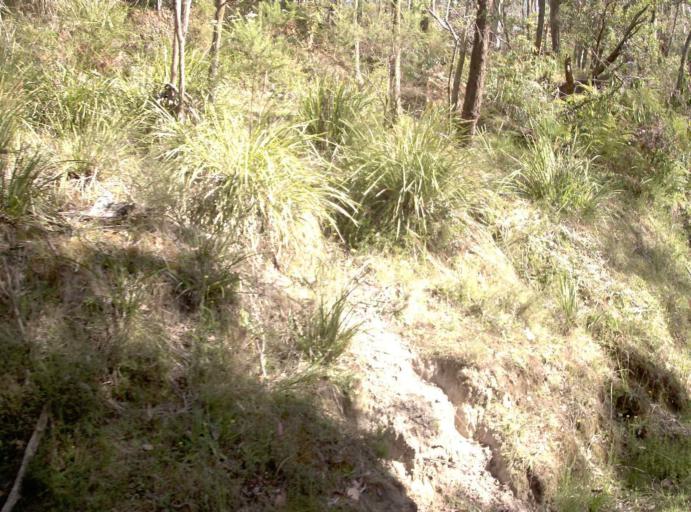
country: AU
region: New South Wales
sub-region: Bombala
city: Bombala
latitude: -37.3603
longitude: 148.6835
